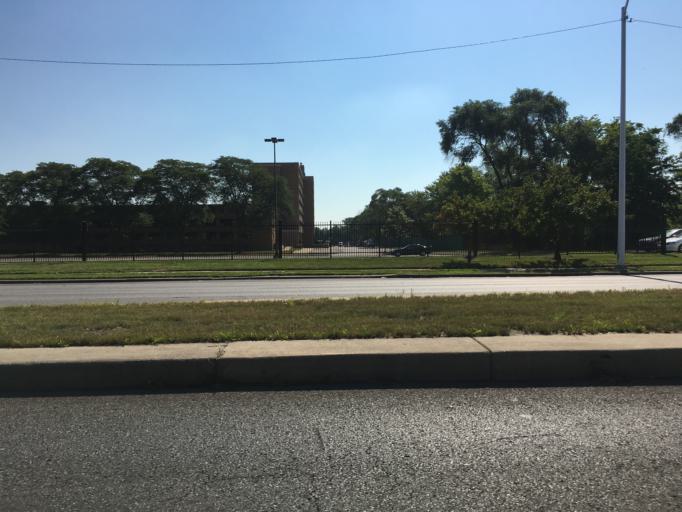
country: US
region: Michigan
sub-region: Wayne County
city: Highland Park
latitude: 42.4111
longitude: -83.1407
